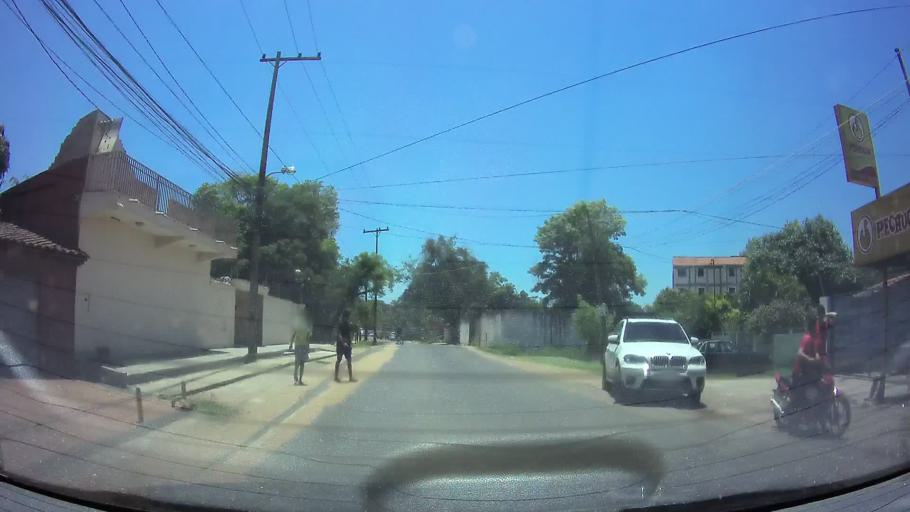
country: PY
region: Central
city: Fernando de la Mora
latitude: -25.2831
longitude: -57.5207
